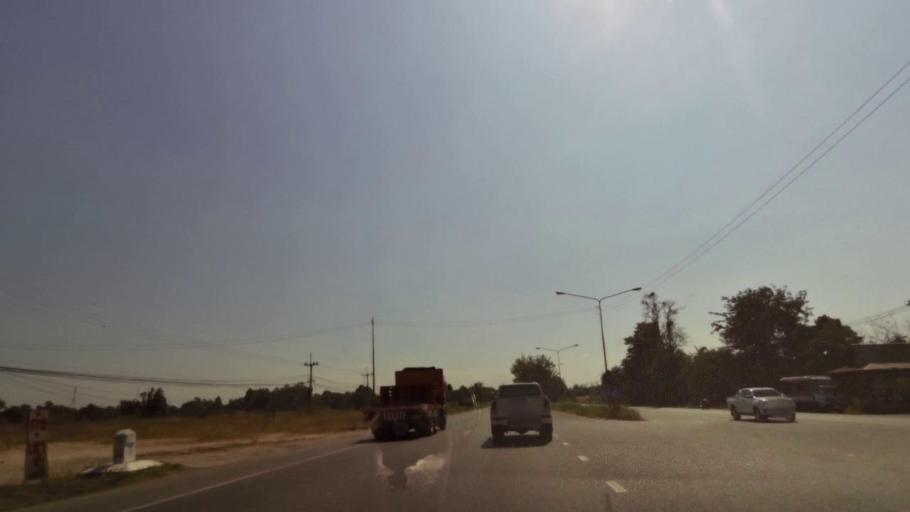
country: TH
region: Nakhon Sawan
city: Kao Liao
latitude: 15.8491
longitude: 100.1172
